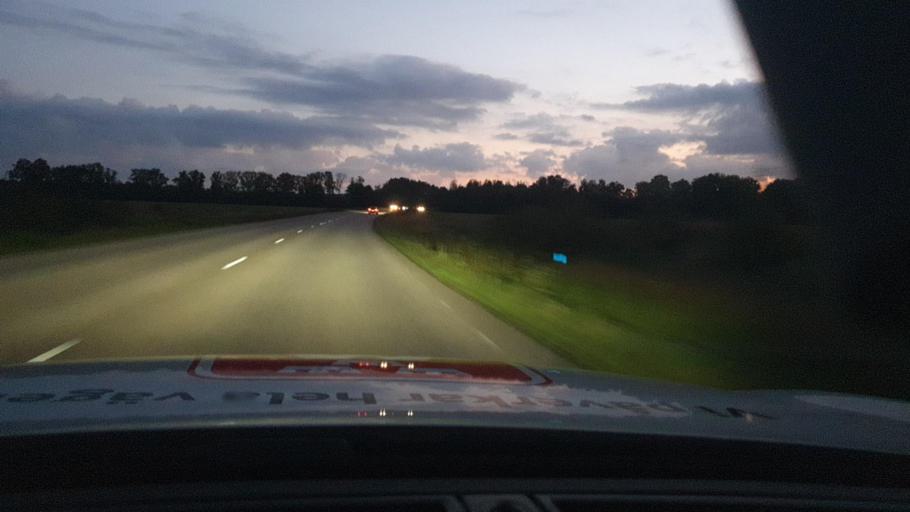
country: SE
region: Skane
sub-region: Angelholms Kommun
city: AEngelholm
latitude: 56.2388
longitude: 12.8921
